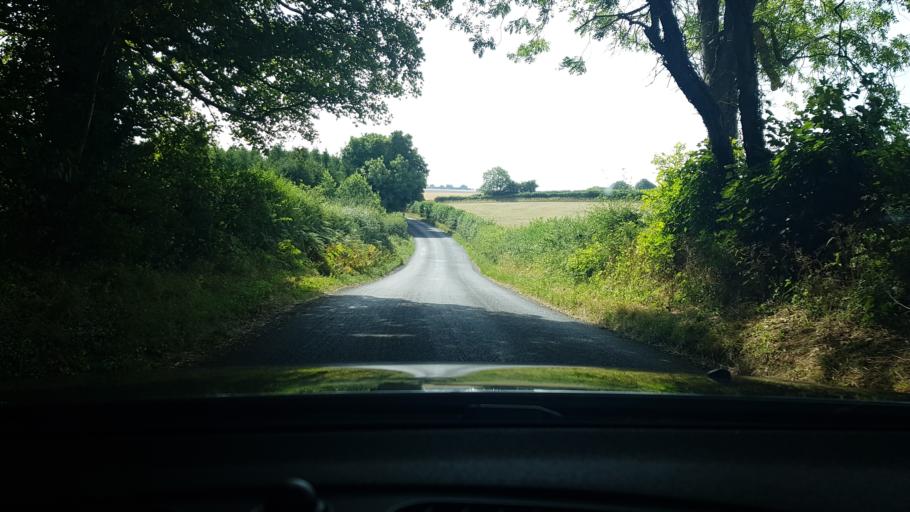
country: GB
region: England
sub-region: Wiltshire
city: Shalbourne
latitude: 51.3643
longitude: -1.5708
